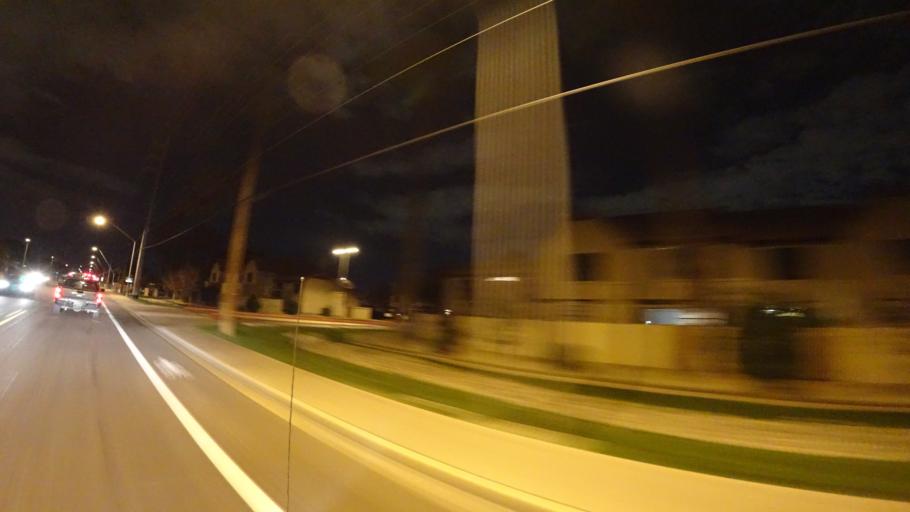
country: US
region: Arizona
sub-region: Maricopa County
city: Mesa
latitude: 33.4194
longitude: -111.8483
